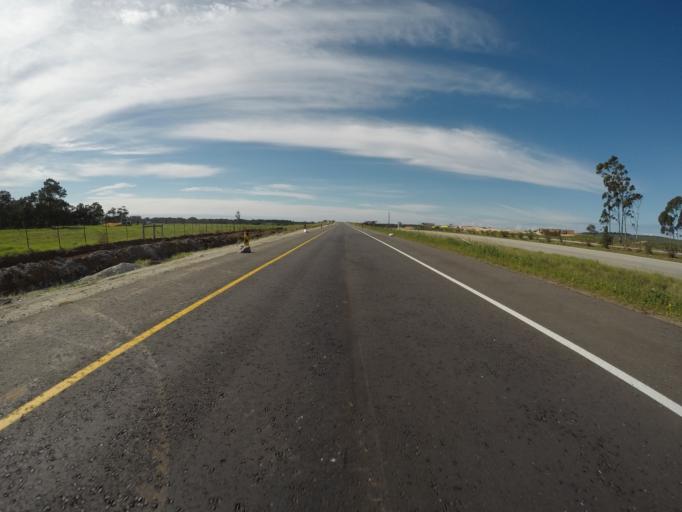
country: ZA
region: Eastern Cape
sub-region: Nelson Mandela Bay Metropolitan Municipality
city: Uitenhage
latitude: -33.9182
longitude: 25.2907
